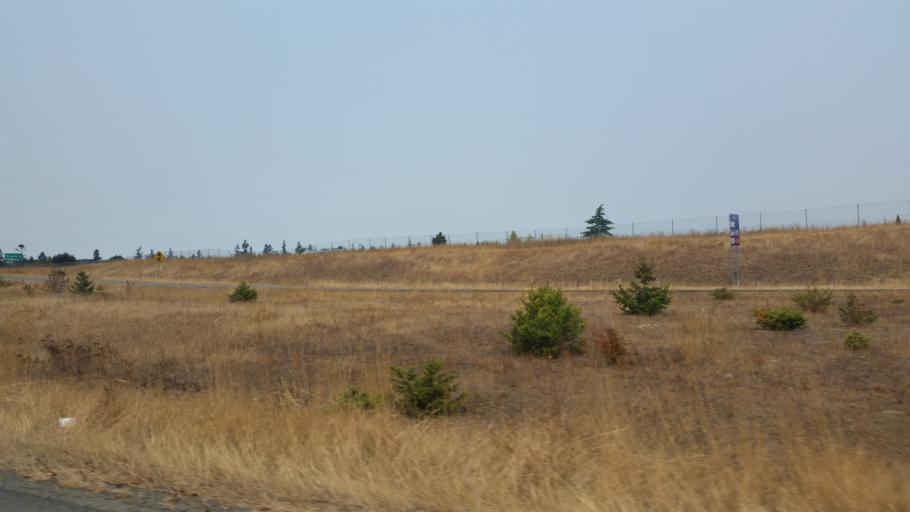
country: US
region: Washington
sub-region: Clallam County
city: Sequim
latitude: 48.0736
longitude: -123.1314
